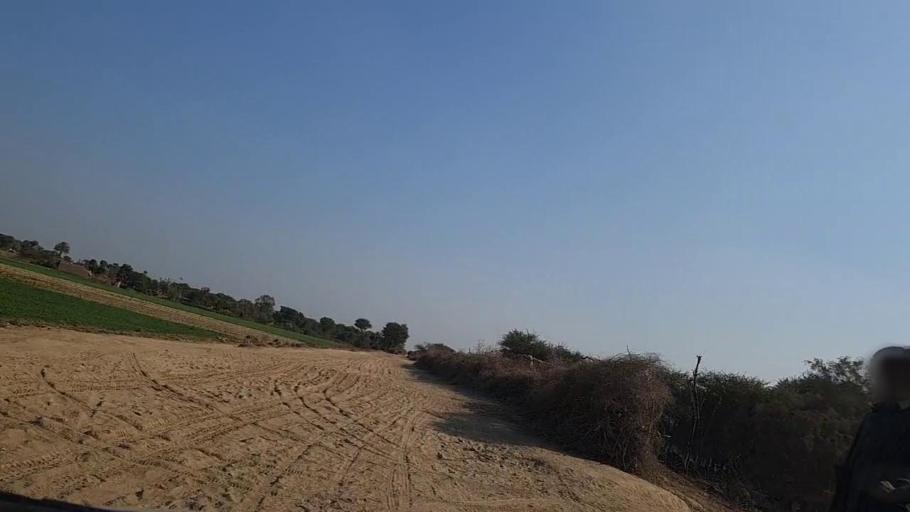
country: PK
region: Sindh
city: Sakrand
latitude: 26.0164
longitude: 68.3136
